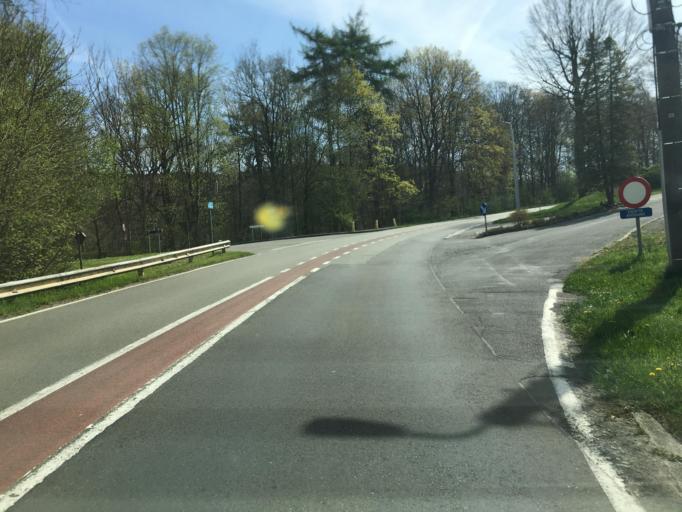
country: BE
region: Wallonia
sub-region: Province de Liege
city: Aywaille
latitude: 50.4307
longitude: 5.6763
